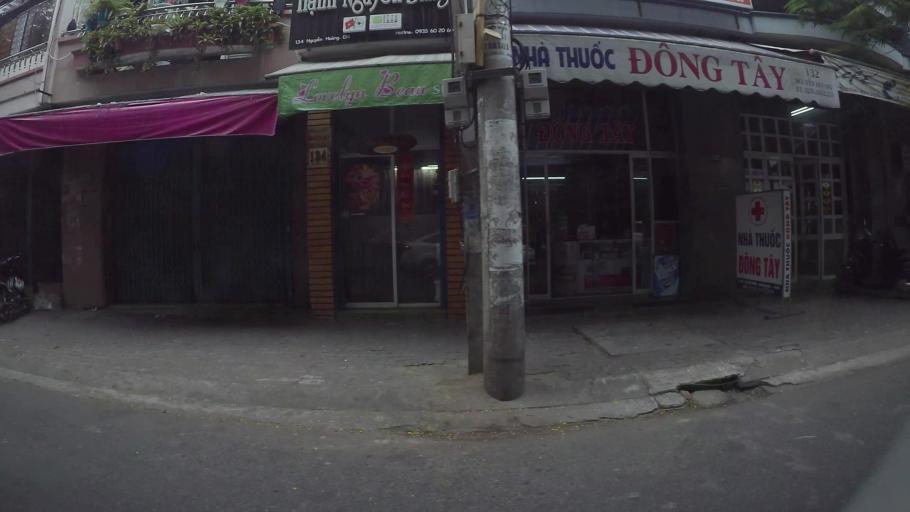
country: VN
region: Da Nang
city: Da Nang
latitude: 16.0623
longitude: 108.2139
